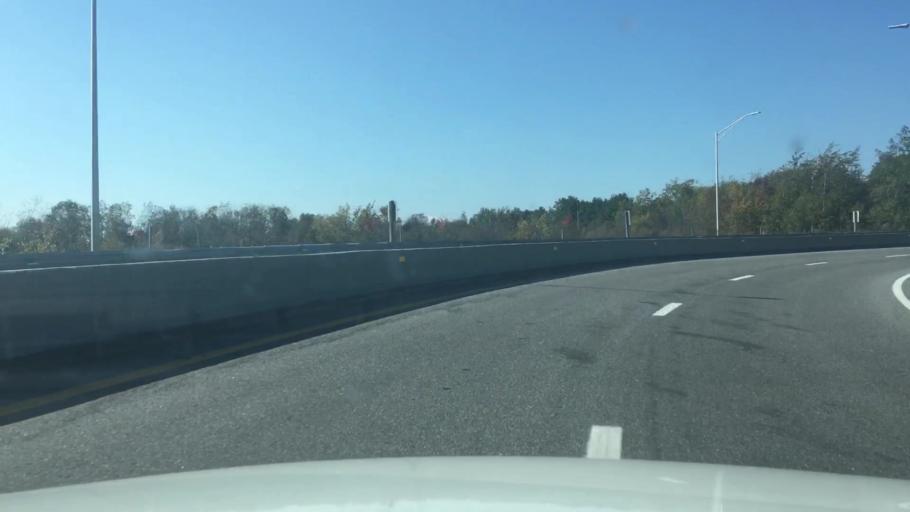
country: US
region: Maine
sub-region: Cumberland County
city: South Portland Gardens
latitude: 43.6479
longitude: -70.3339
